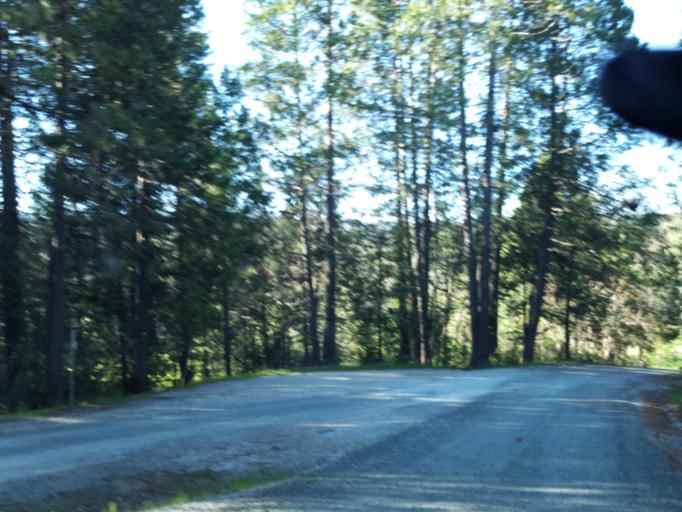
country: US
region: California
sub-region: Amador County
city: Pine Grove
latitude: 38.4336
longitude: -120.6268
